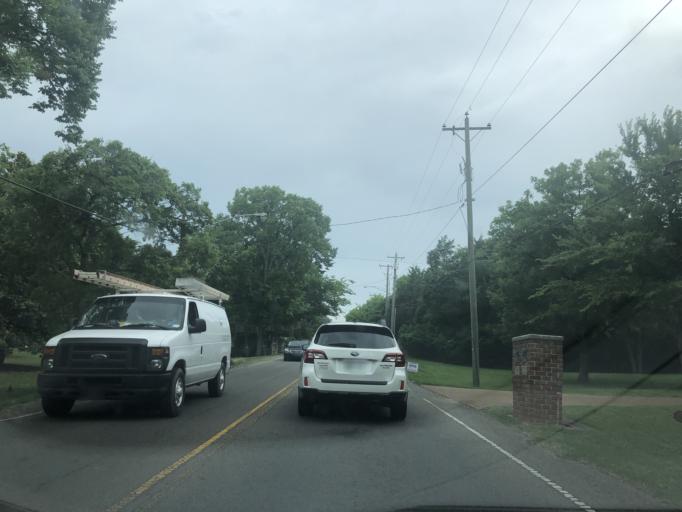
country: US
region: Tennessee
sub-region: Davidson County
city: Oak Hill
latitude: 36.0892
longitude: -86.8006
